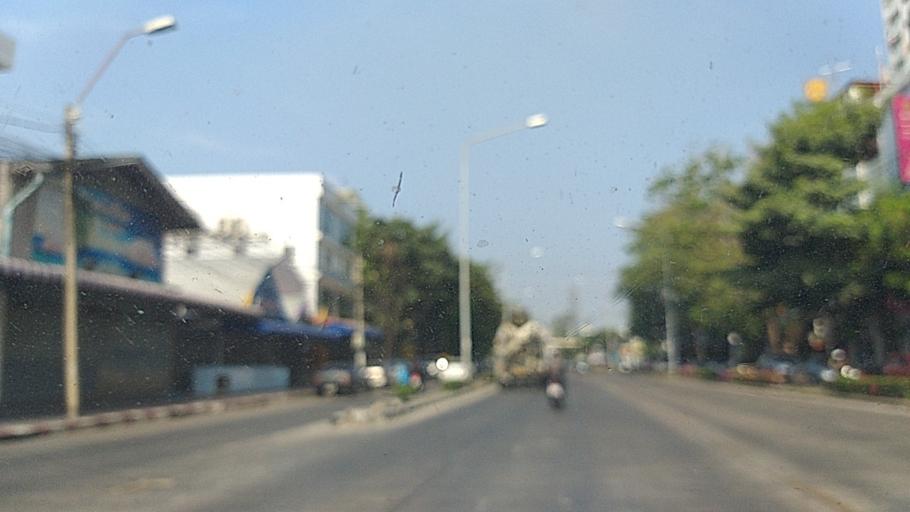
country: TH
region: Bangkok
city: Chatuchak
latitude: 13.8401
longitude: 100.5480
